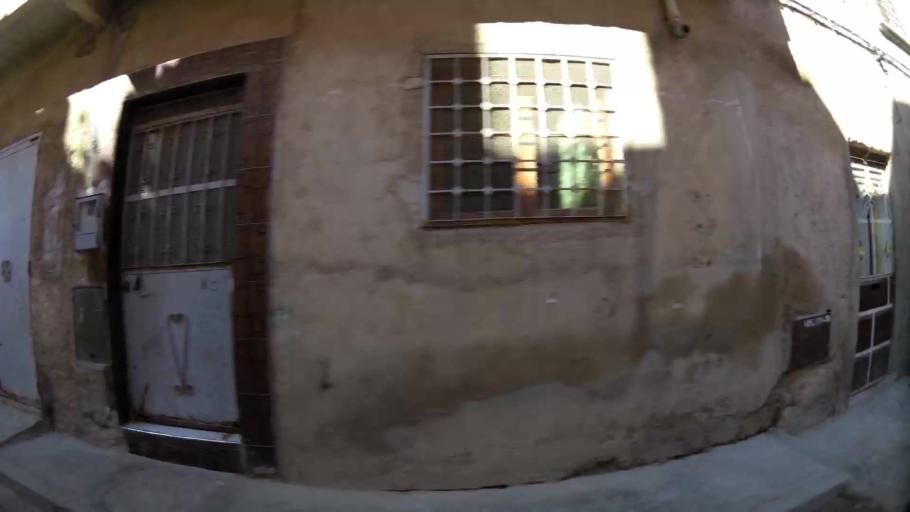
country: MA
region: Oriental
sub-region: Oujda-Angad
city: Oujda
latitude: 34.6488
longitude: -1.9455
